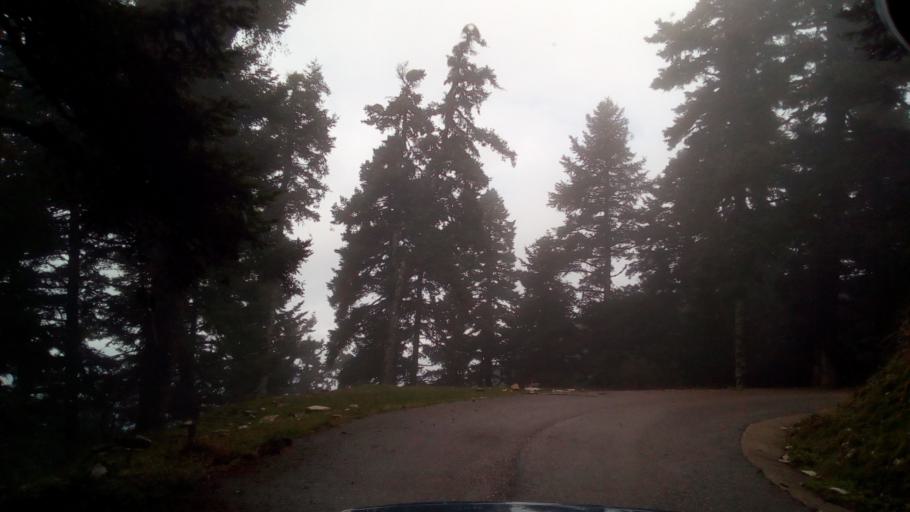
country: GR
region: West Greece
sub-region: Nomos Aitolias kai Akarnanias
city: Nafpaktos
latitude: 38.5399
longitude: 21.8562
